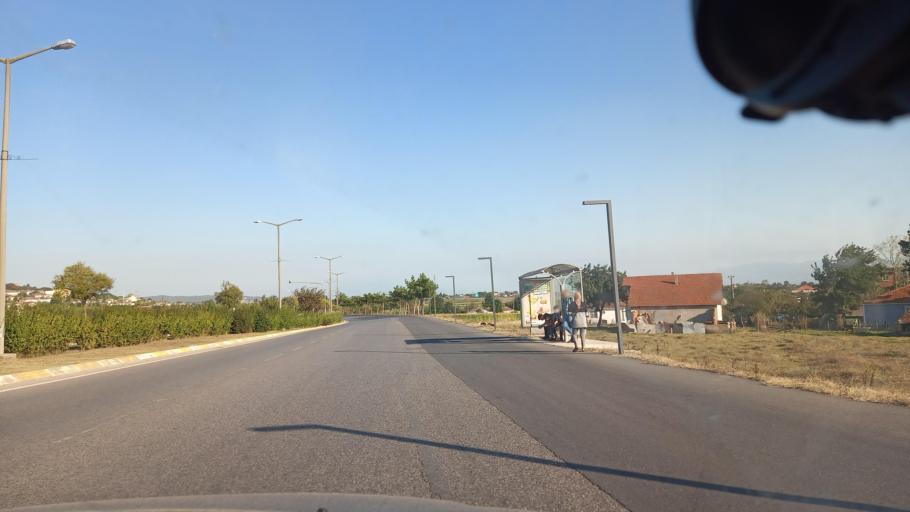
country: TR
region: Sakarya
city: Kazimpasa
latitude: 40.8504
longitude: 30.3170
